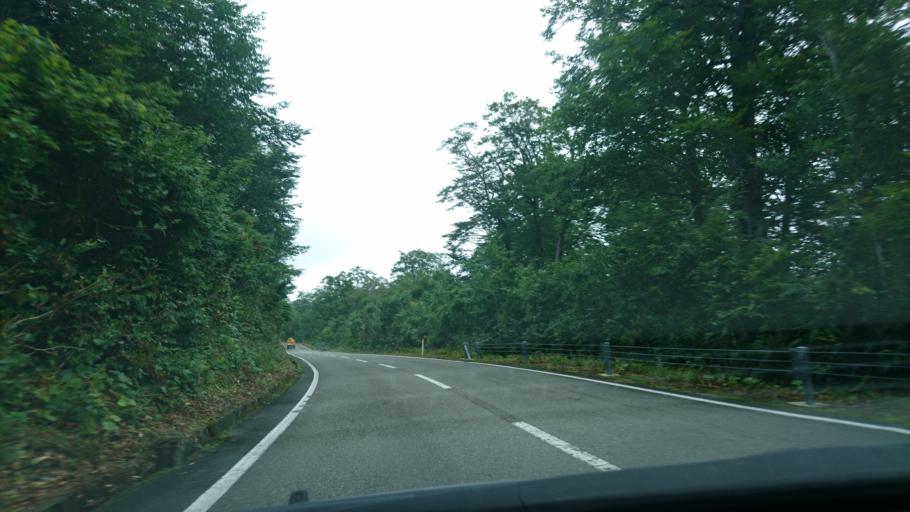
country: JP
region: Akita
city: Yuzawa
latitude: 38.9814
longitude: 140.7435
